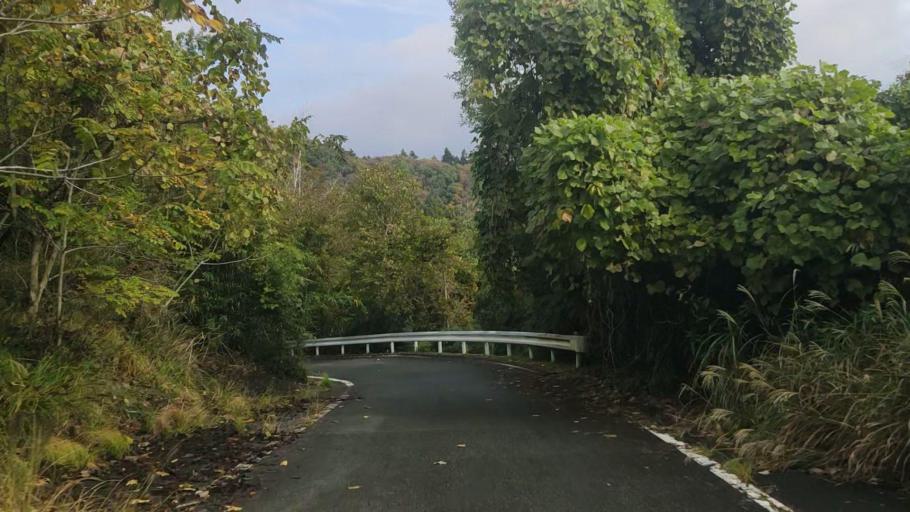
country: JP
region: Shizuoka
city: Fujinomiya
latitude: 35.3297
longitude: 138.4411
